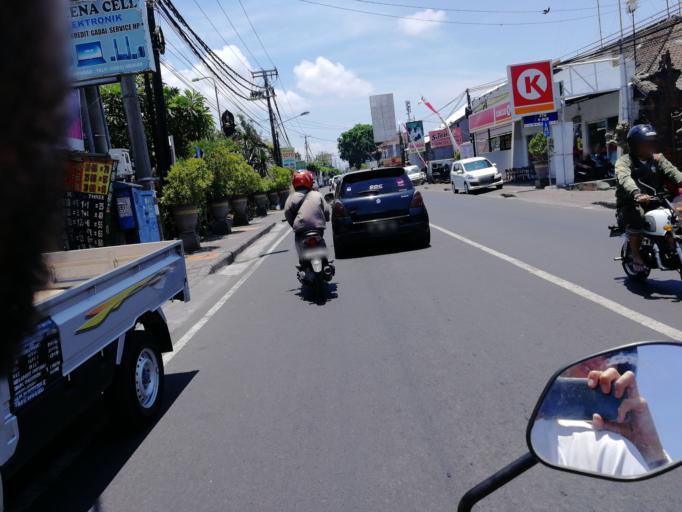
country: ID
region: Bali
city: Karyadharma
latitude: -8.6860
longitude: 115.1938
